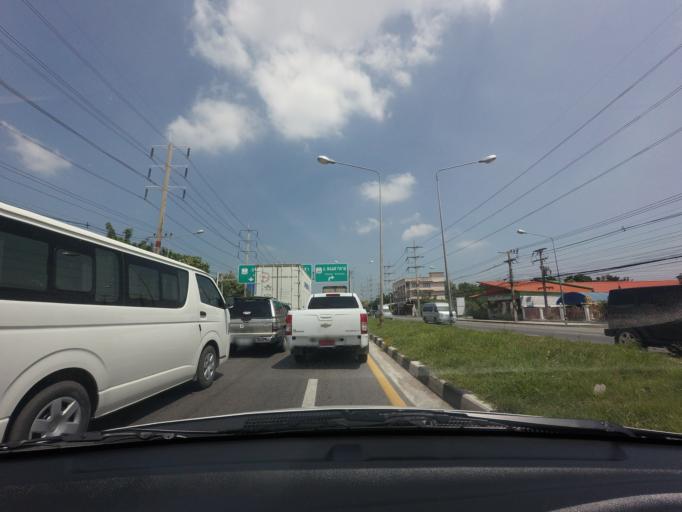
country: TH
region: Chachoengsao
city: Chachoengsao
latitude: 13.6571
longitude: 101.0480
